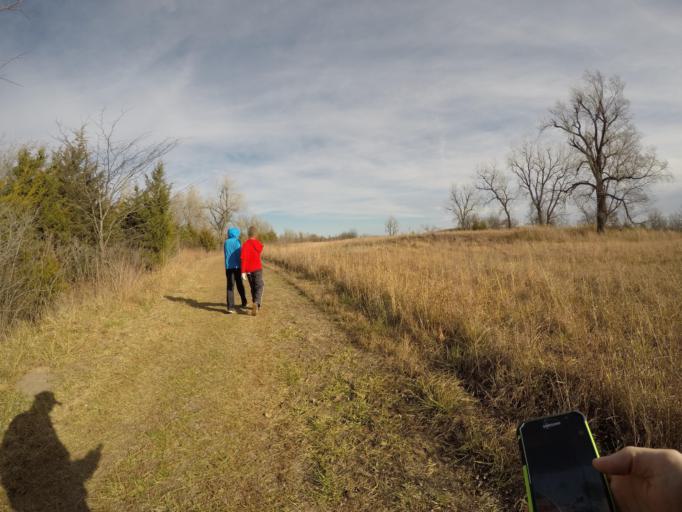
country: US
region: Kansas
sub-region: Reno County
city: Buhler
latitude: 38.1168
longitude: -97.8558
